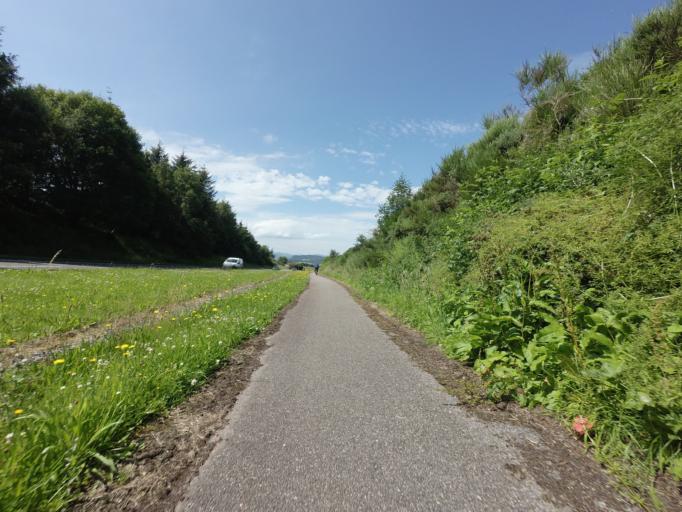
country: GB
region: Scotland
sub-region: Highland
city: Conon Bridge
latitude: 57.5510
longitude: -4.4025
